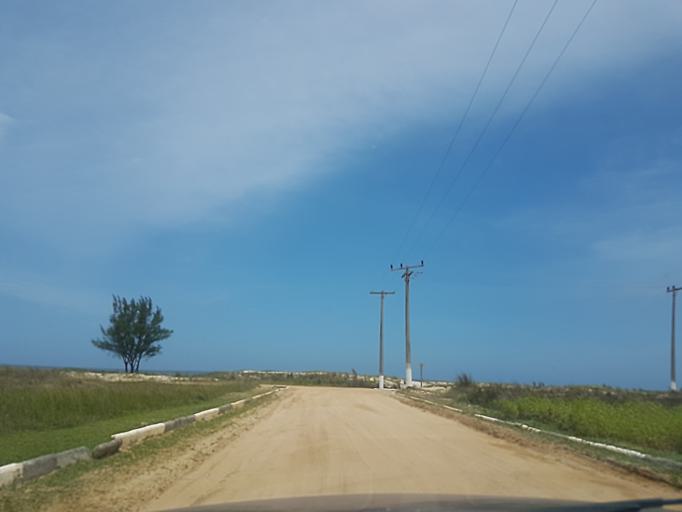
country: BR
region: Santa Catarina
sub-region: Jaguaruna
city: Jaguaruna
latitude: -28.6639
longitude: -48.9629
